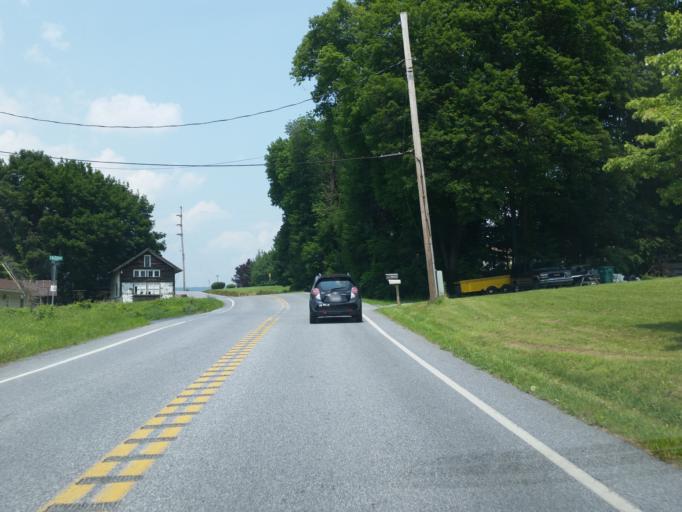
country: US
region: Pennsylvania
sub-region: Lebanon County
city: Palmyra
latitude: 40.3732
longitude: -76.6354
